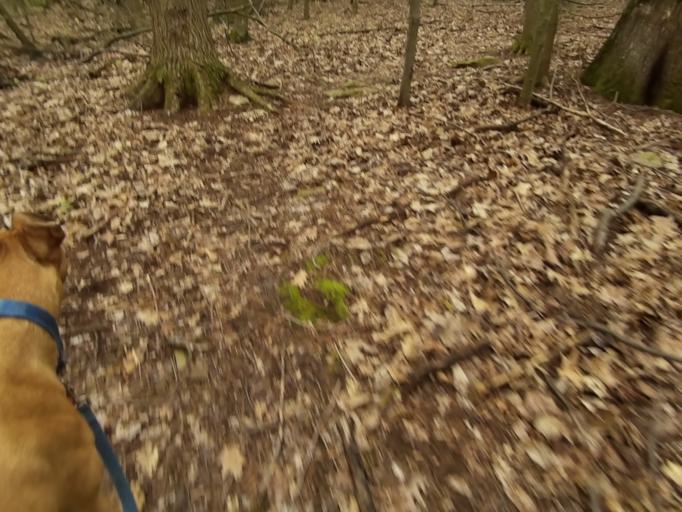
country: US
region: Pennsylvania
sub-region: Centre County
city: Boalsburg
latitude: 40.7586
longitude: -77.8217
